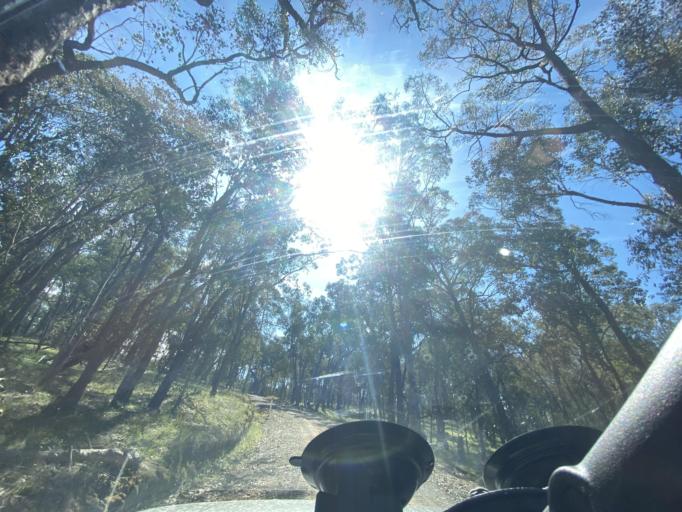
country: AU
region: Victoria
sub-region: Mansfield
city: Mansfield
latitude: -36.8029
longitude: 146.1209
